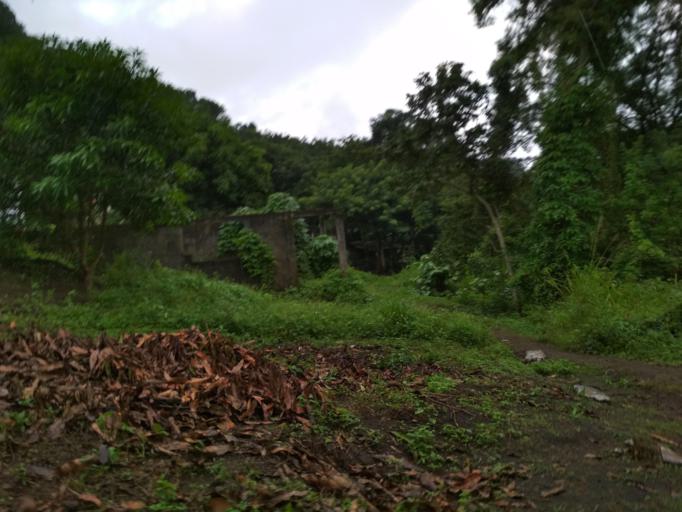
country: MX
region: Veracruz
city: San Andres Tuxtla
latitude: 18.4512
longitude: -95.1979
